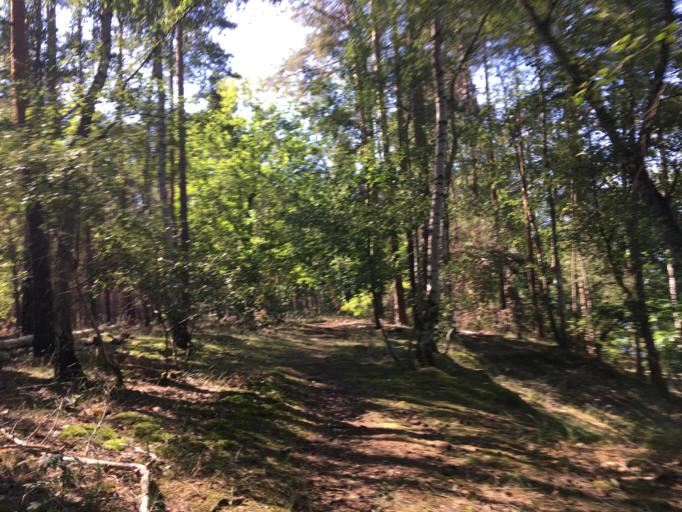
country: DE
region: Brandenburg
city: Gross Koris
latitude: 52.2025
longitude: 13.7418
